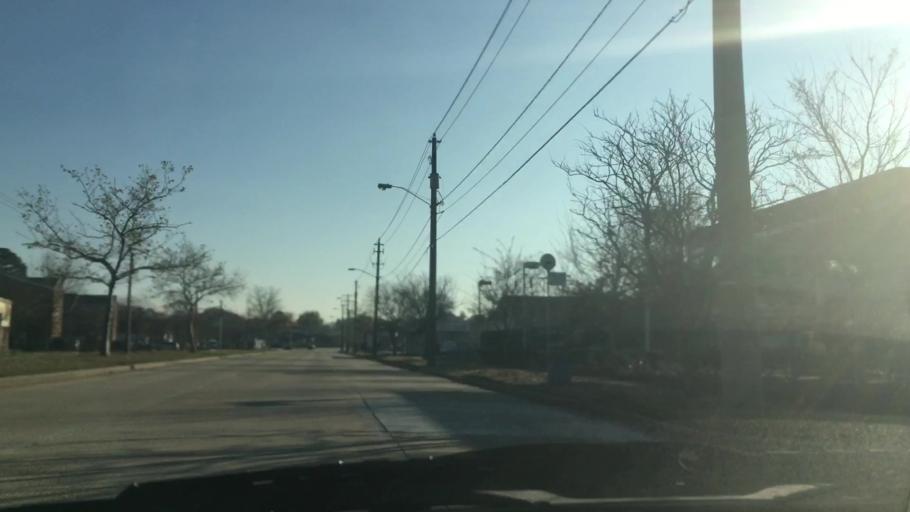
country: US
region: Virginia
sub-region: City of Norfolk
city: Norfolk
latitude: 36.8937
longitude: -76.2382
